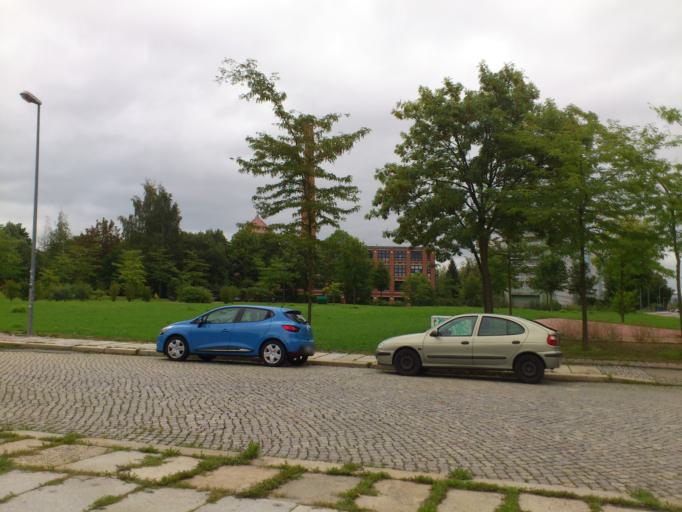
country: DE
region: Saxony
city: Chemnitz
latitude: 50.8391
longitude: 12.9164
